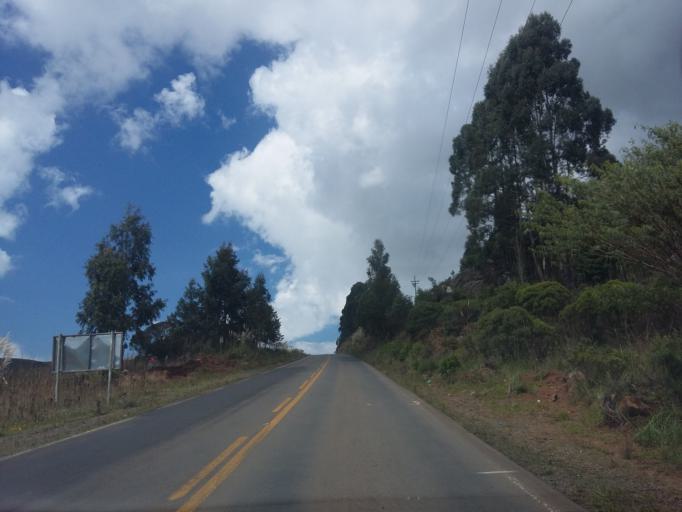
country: BR
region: Santa Catarina
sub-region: Lauro Muller
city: Lauro Muller
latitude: -28.3501
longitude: -49.5975
